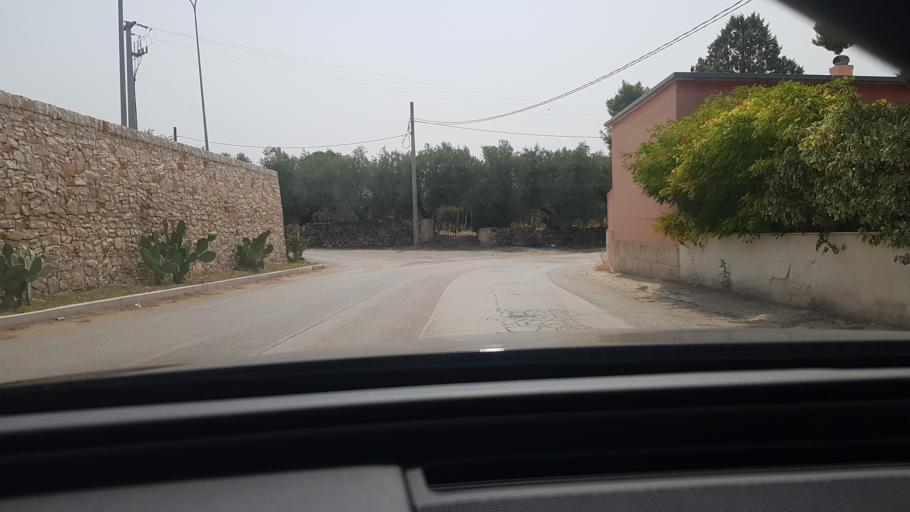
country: IT
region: Apulia
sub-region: Provincia di Barletta - Andria - Trani
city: Andria
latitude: 41.2289
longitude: 16.2687
